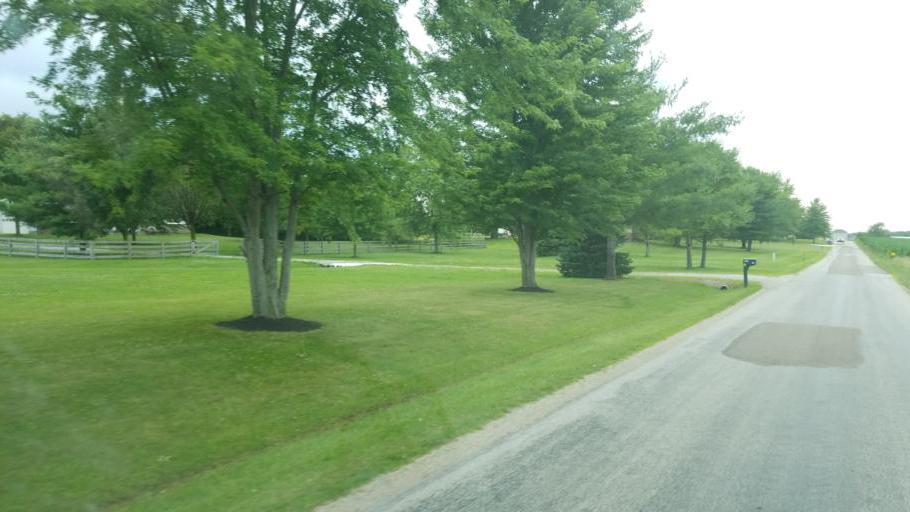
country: US
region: Ohio
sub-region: Knox County
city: Centerburg
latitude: 40.2932
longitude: -82.7396
